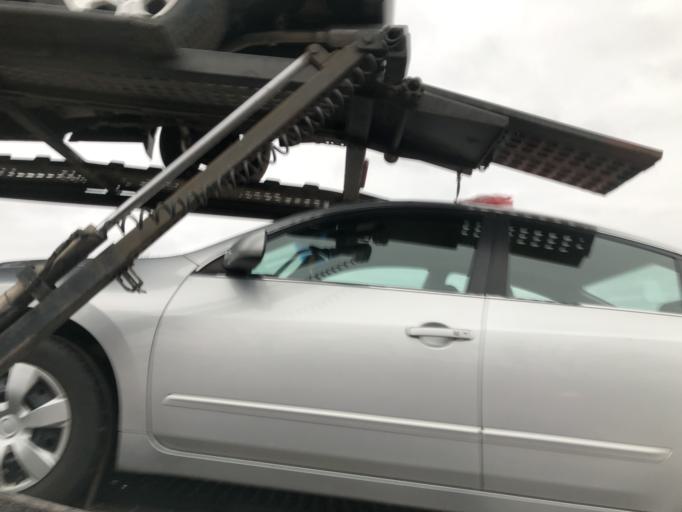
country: US
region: Illinois
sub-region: Johnson County
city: Vienna
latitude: 37.3751
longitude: -88.8143
